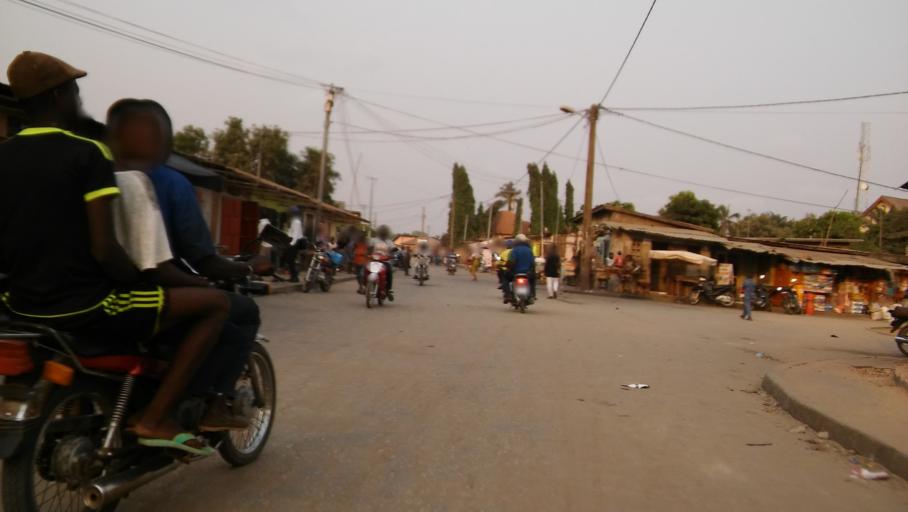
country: BJ
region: Atlantique
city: Abomey-Calavi
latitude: 6.3889
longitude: 2.3455
